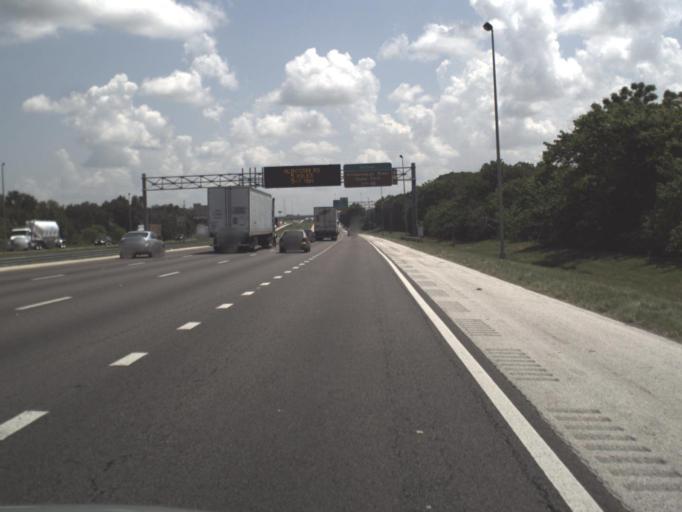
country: US
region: Florida
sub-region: Hillsborough County
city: Mango
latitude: 28.0034
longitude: -82.3159
